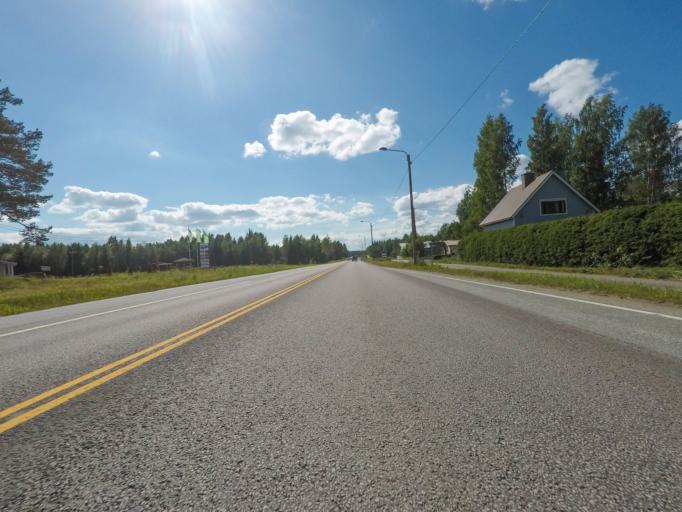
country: FI
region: Southern Savonia
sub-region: Savonlinna
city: Savonlinna
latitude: 61.8811
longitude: 29.0448
